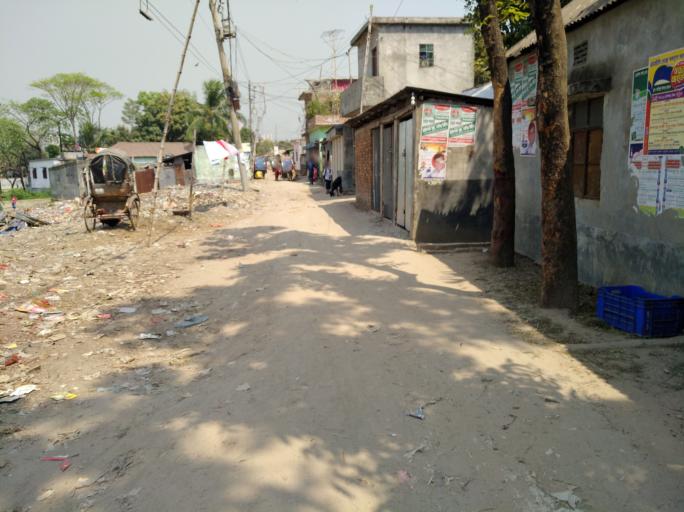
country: BD
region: Dhaka
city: Tungi
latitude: 23.9216
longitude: 90.4002
